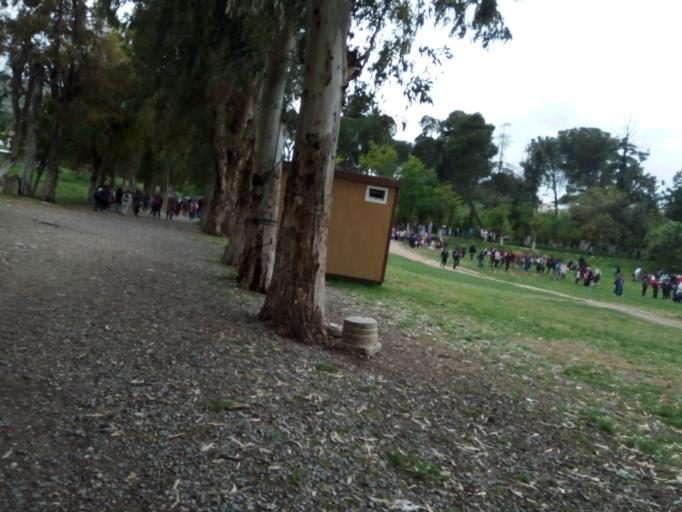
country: DZ
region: Setif
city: El Eulma
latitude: 36.3178
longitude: 5.7375
